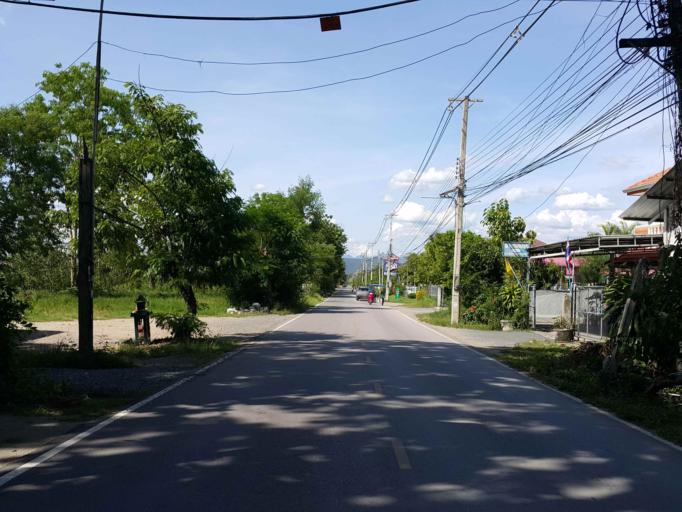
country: TH
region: Chiang Mai
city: San Kamphaeng
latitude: 18.7615
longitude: 99.1417
